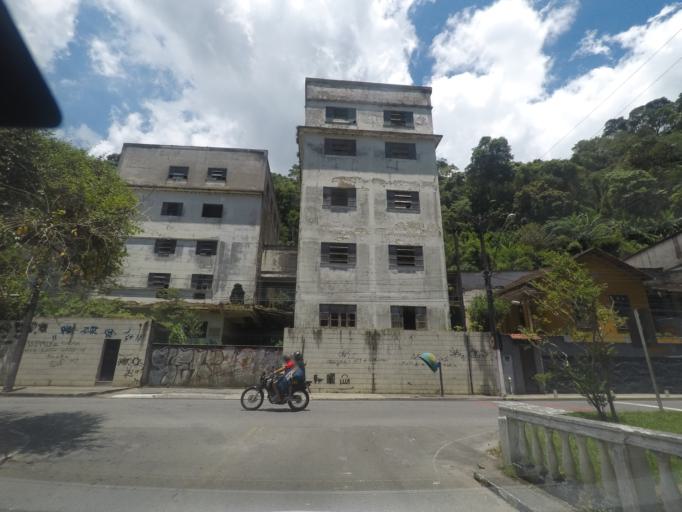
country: BR
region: Rio de Janeiro
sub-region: Petropolis
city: Petropolis
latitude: -22.4936
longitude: -43.1796
